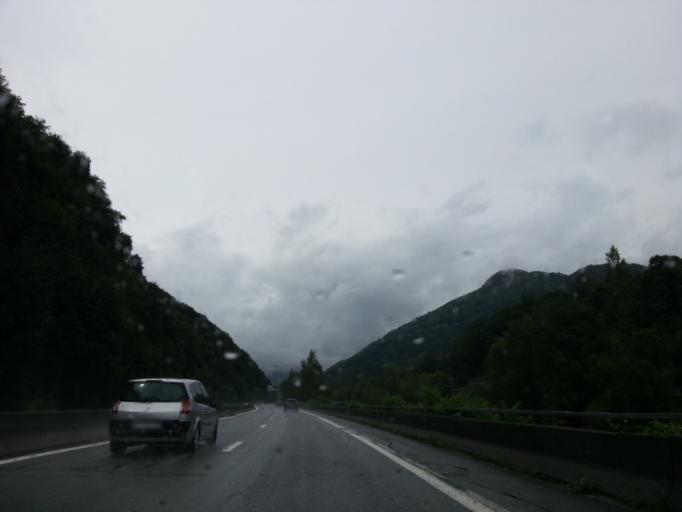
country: FR
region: Rhone-Alpes
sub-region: Departement de la Savoie
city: Albertville
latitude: 45.6901
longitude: 6.4008
